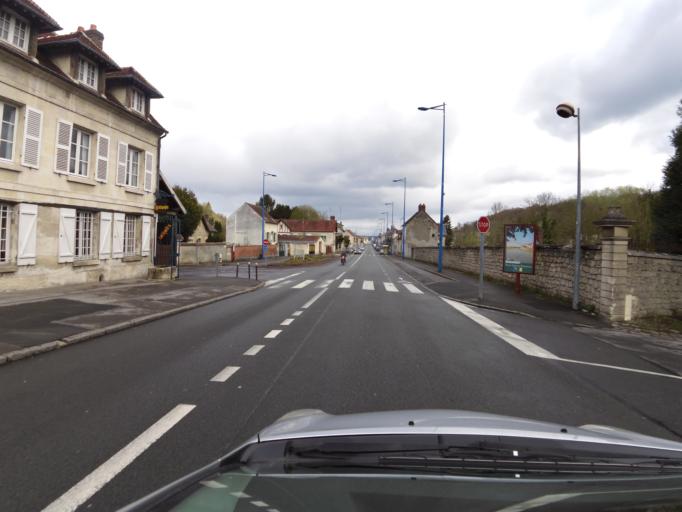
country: FR
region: Picardie
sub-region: Departement de l'Oise
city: Pont-Sainte-Maxence
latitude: 49.2928
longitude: 2.6048
